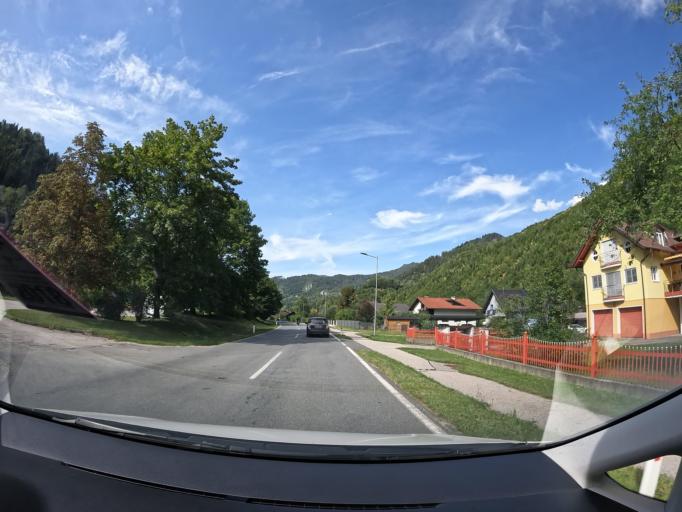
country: AT
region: Carinthia
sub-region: Politischer Bezirk Volkermarkt
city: Bad Eisenkappel
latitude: 46.4751
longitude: 14.5928
